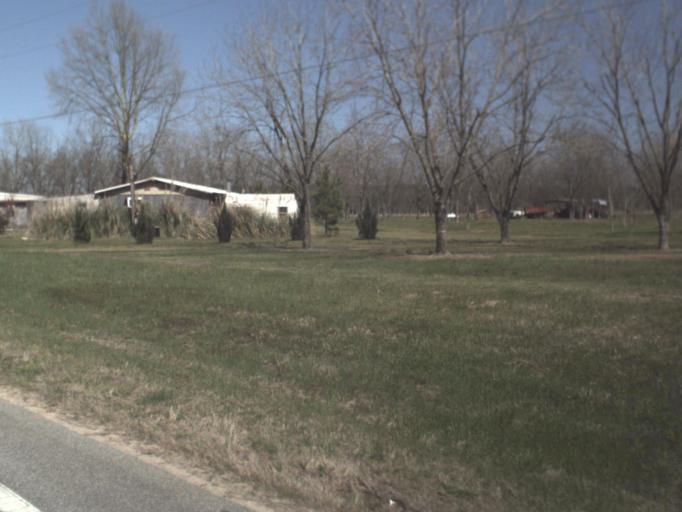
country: US
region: Florida
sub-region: Gadsden County
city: Gretna
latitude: 30.7001
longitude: -84.6251
